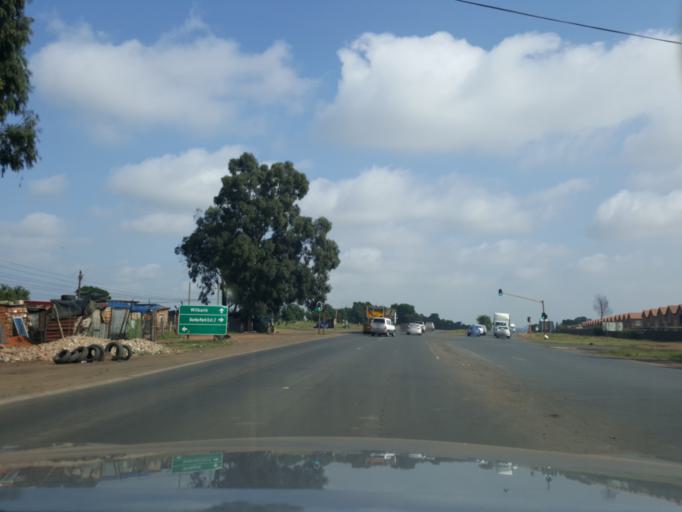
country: ZA
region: Mpumalanga
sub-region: Nkangala District Municipality
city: Witbank
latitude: -25.9520
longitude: 29.2494
